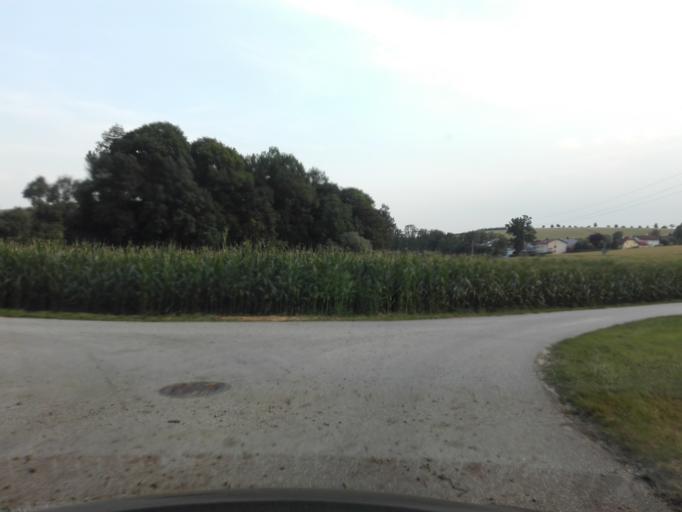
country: AT
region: Upper Austria
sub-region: Politischer Bezirk Grieskirchen
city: Grieskirchen
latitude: 48.2510
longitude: 13.8138
